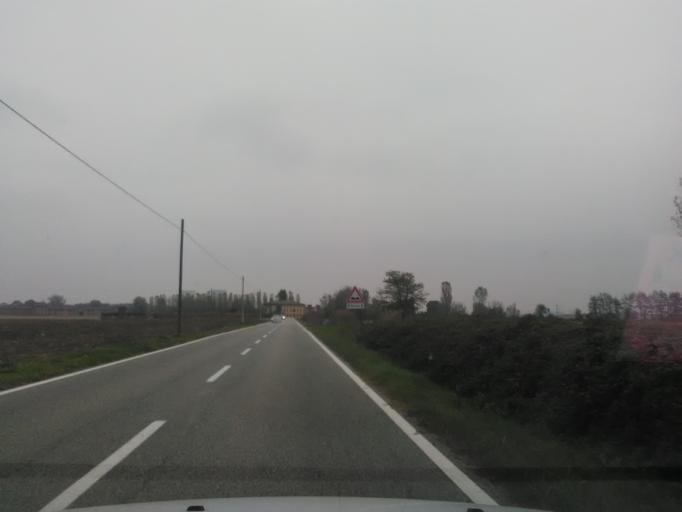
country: IT
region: Piedmont
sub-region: Provincia di Vercelli
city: Bianze
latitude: 45.2568
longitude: 8.1623
